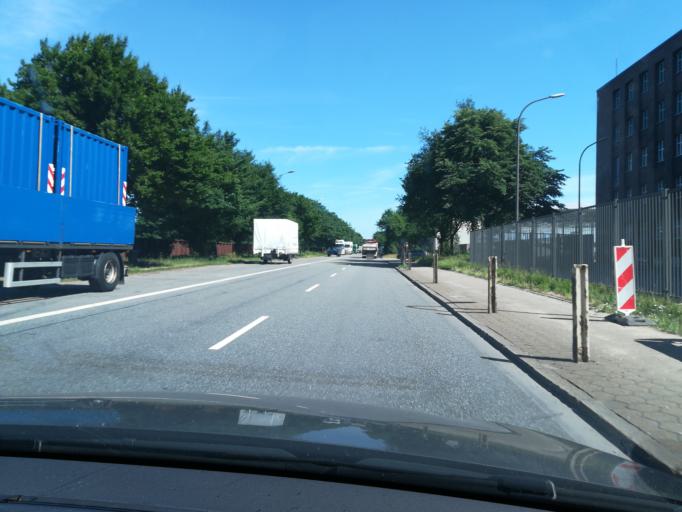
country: DE
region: Hamburg
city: Rothenburgsort
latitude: 53.5237
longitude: 10.0366
